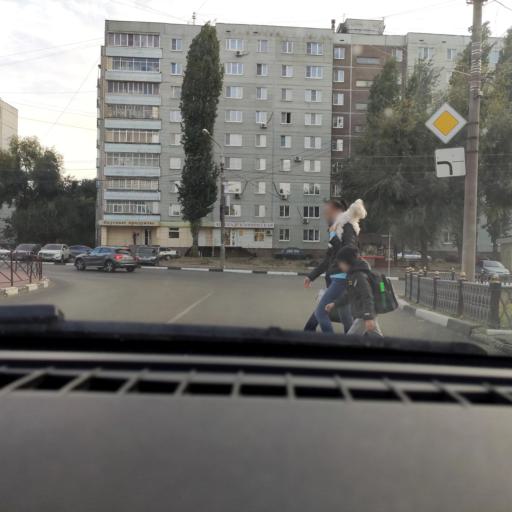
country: RU
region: Voronezj
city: Voronezh
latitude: 51.6744
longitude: 39.2495
